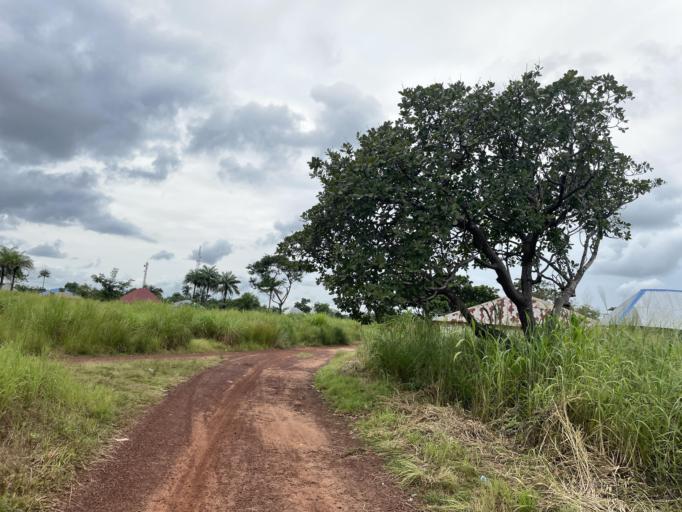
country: SL
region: Northern Province
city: Kambia
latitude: 9.1266
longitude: -12.9013
